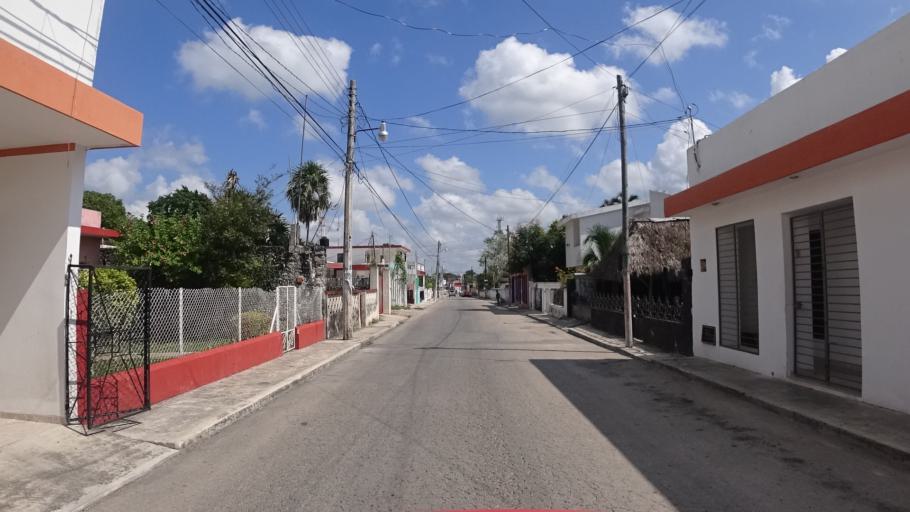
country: MX
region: Yucatan
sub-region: Tizimin
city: Tizimin
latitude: 21.1379
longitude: -88.1533
